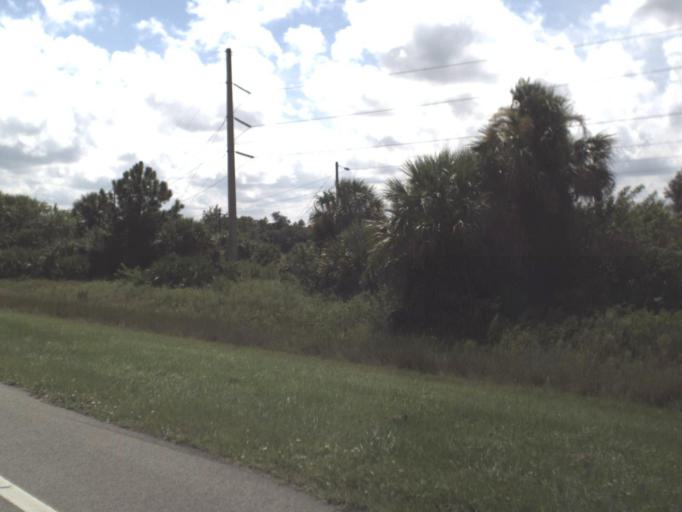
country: US
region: Florida
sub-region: Collier County
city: Immokalee
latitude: 26.3640
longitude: -81.3479
